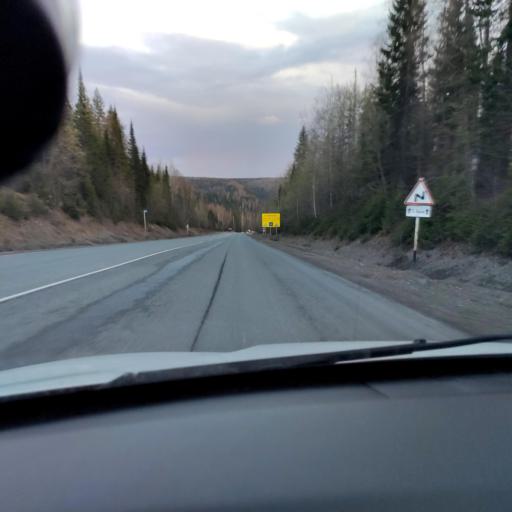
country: RU
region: Perm
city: Gremyachinsk
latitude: 58.4501
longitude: 57.8720
